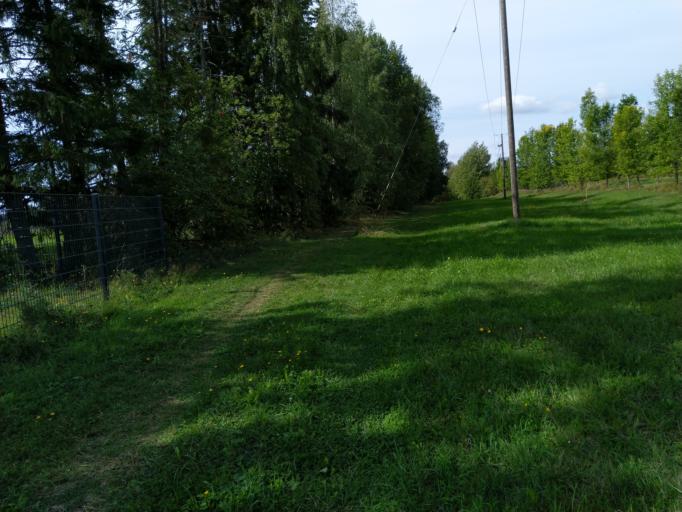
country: FI
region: Varsinais-Suomi
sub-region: Salo
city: Halikko
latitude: 60.3961
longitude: 23.0748
